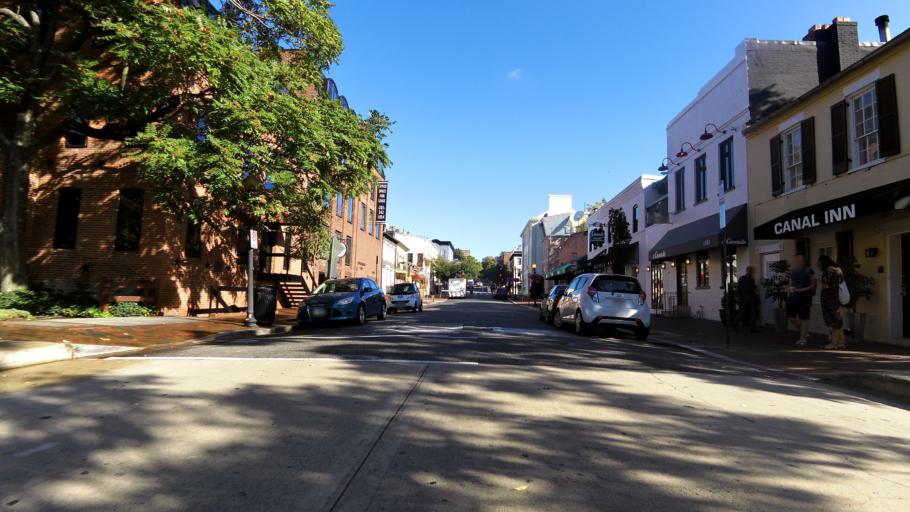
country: US
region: Washington, D.C.
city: Washington, D.C.
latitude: 38.9042
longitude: -77.0612
